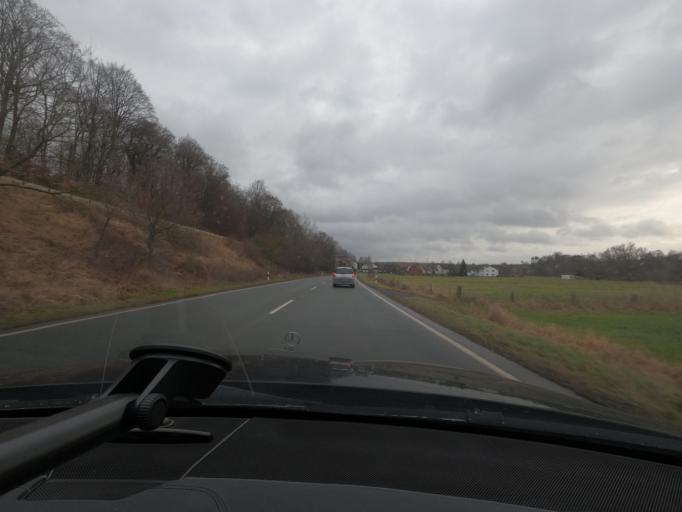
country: DE
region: Hesse
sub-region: Regierungsbezirk Kassel
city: Volkmarsen
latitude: 51.3895
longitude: 9.1432
